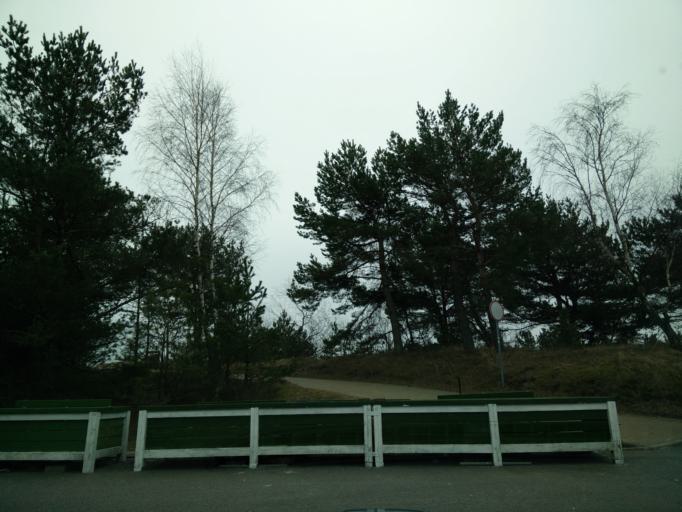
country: LT
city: Nida
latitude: 55.2952
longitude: 20.9868
